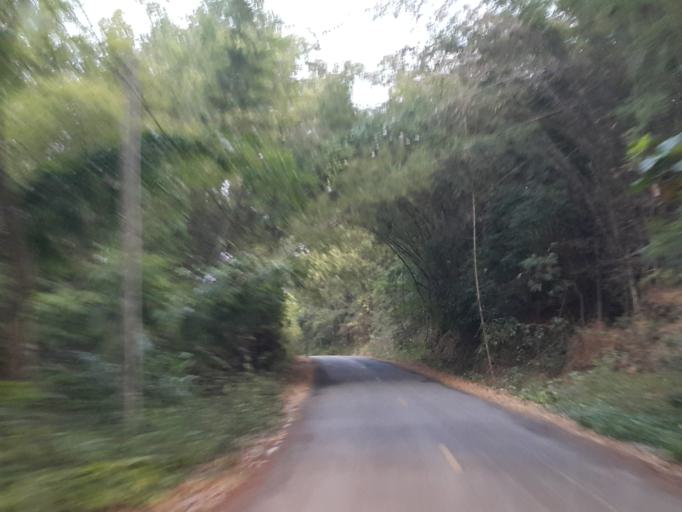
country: TH
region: Lampang
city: Mueang Pan
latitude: 18.8284
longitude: 99.4592
